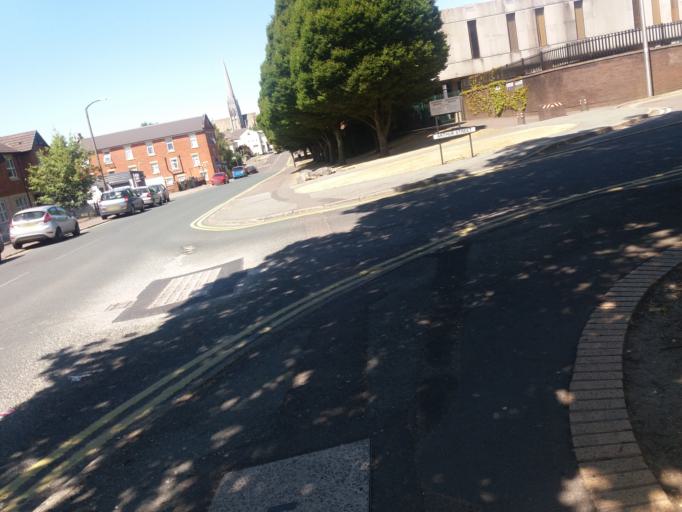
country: GB
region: England
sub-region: Lancashire
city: Preston
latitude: 53.7577
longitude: -2.7112
